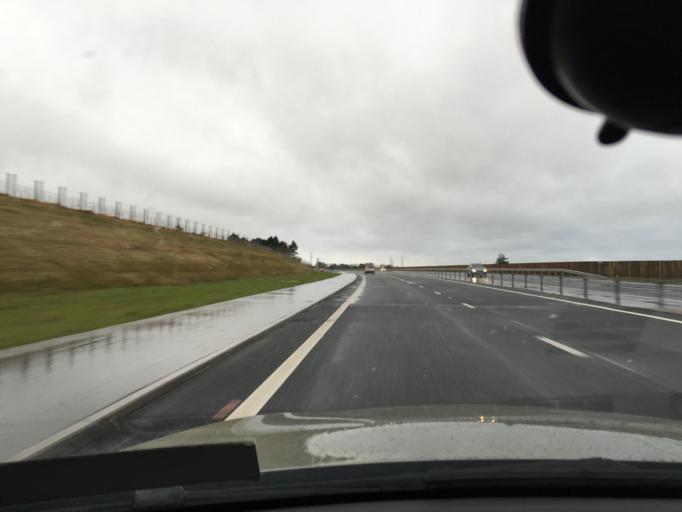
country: GB
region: Northern Ireland
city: Ballyclare
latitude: 54.7954
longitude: -5.9315
